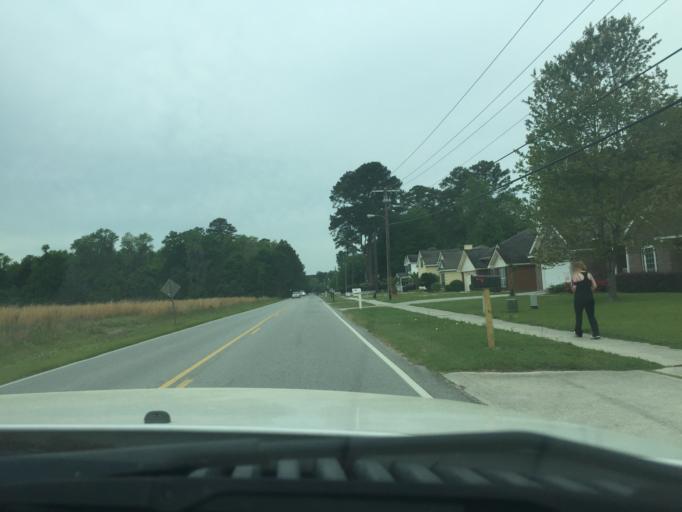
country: US
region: Georgia
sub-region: Chatham County
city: Georgetown
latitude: 31.9693
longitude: -81.2346
